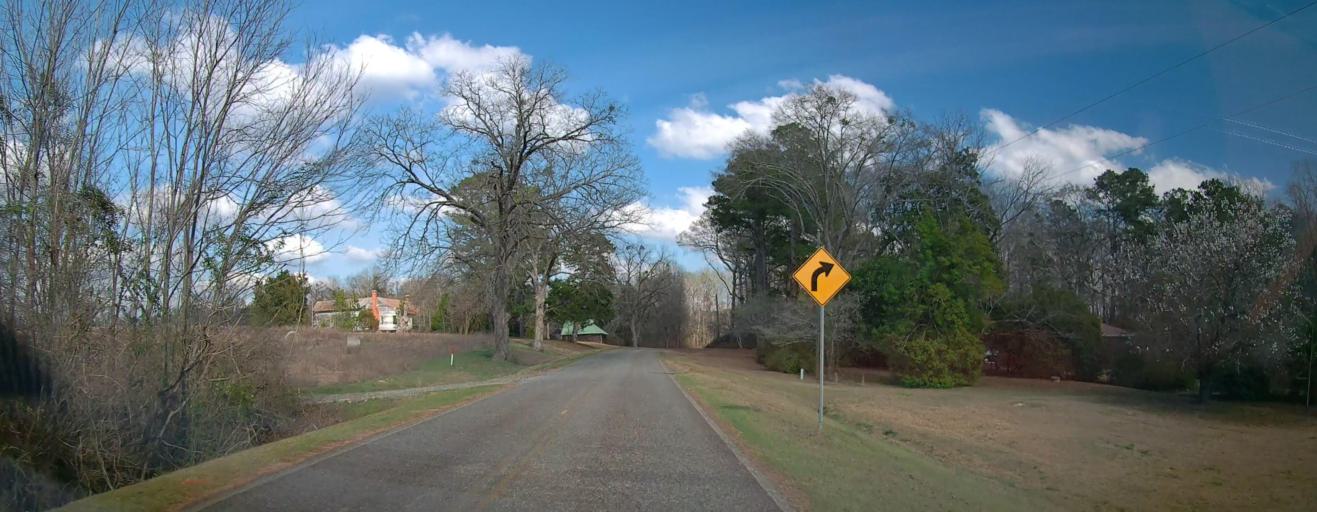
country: US
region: Georgia
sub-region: Wilkinson County
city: Irwinton
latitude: 32.6409
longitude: -83.1751
